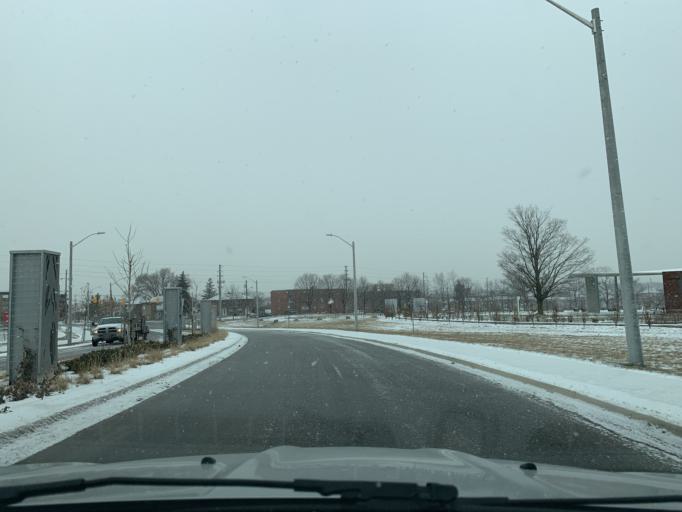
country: CA
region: Ontario
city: Concord
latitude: 43.7368
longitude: -79.4826
